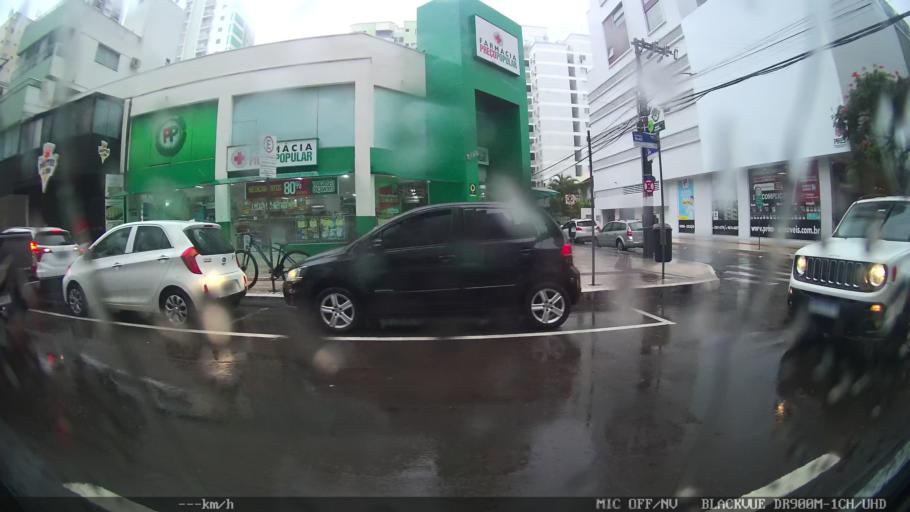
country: BR
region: Santa Catarina
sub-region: Balneario Camboriu
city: Balneario Camboriu
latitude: -26.9955
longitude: -48.6284
